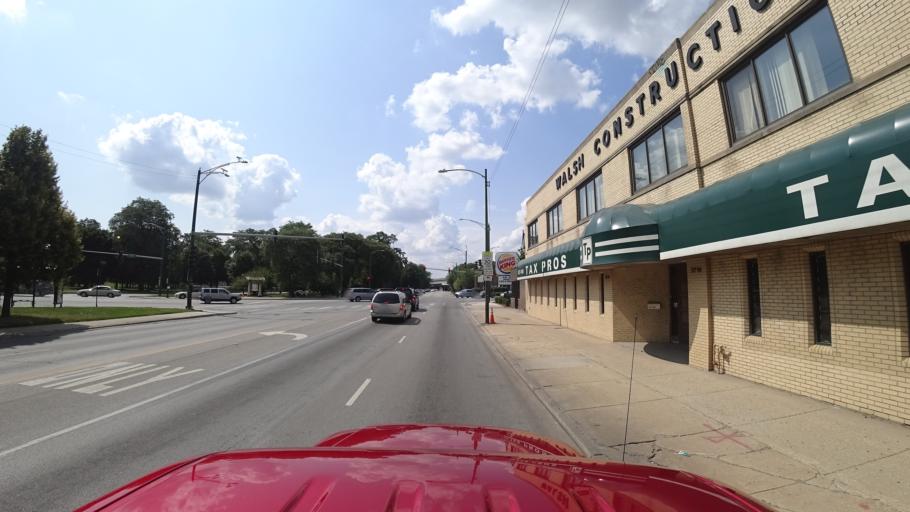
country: US
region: Illinois
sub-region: Cook County
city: Chicago
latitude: 41.8265
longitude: -87.6850
